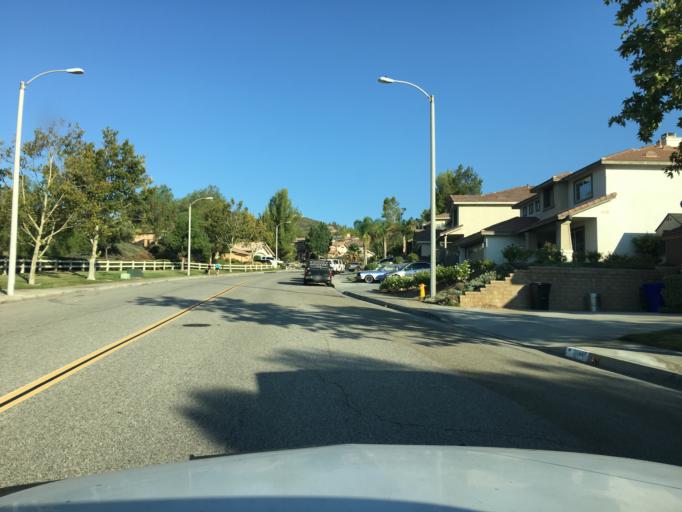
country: US
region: California
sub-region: Los Angeles County
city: Castaic
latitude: 34.5084
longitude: -118.6343
